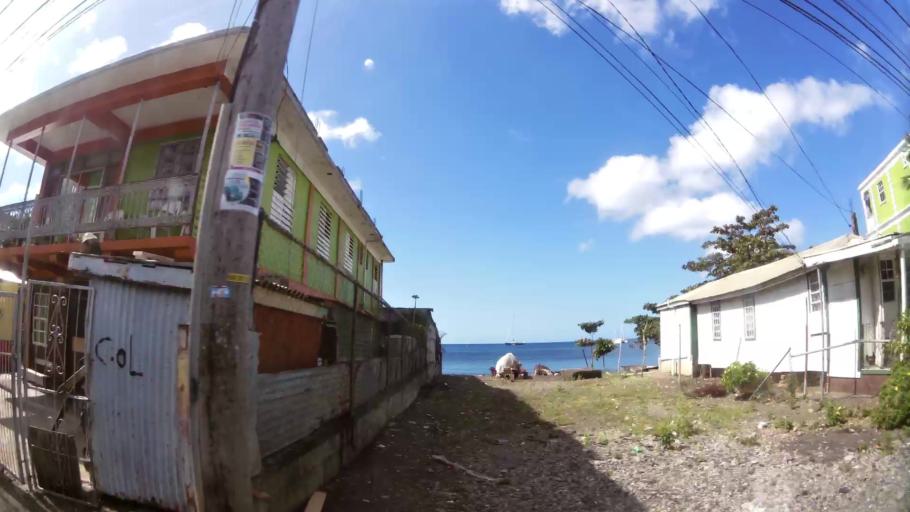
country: DM
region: Saint John
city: Portsmouth
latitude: 15.5786
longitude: -61.4578
